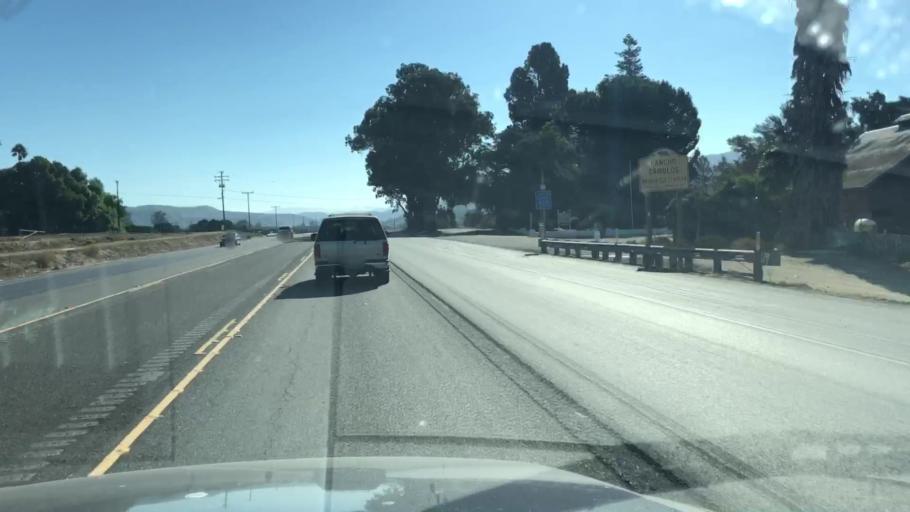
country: US
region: California
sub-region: Ventura County
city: Piru
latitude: 34.4069
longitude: -118.7578
